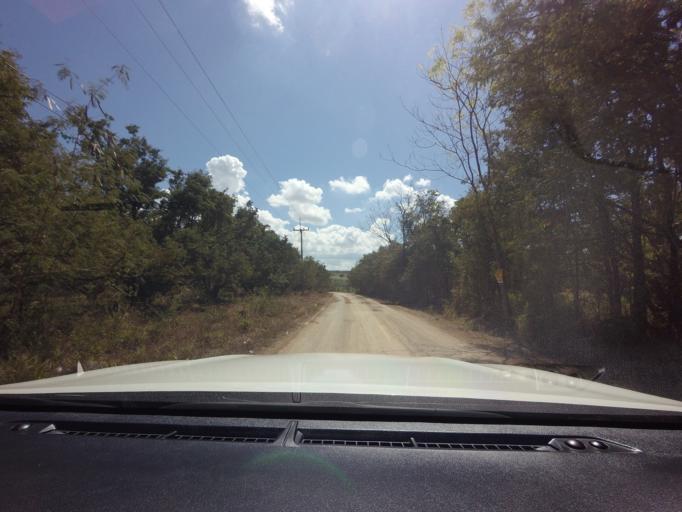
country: TH
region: Nakhon Ratchasima
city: Wang Nam Khiao
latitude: 14.4385
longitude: 101.6950
